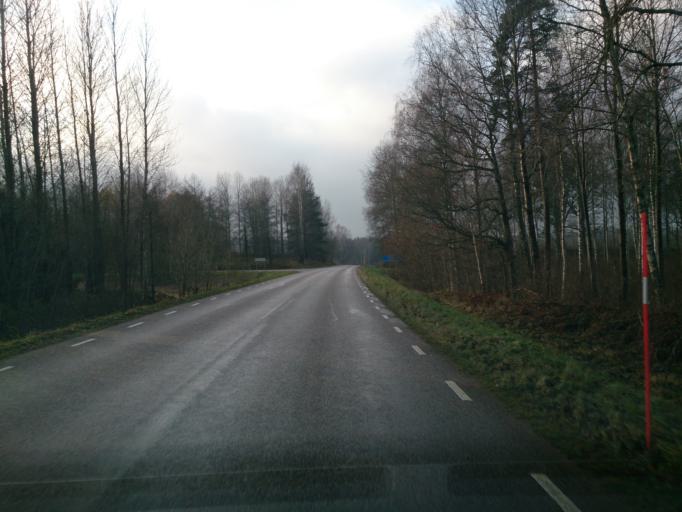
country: SE
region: OEstergoetland
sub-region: Atvidabergs Kommun
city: Atvidaberg
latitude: 58.2216
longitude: 15.9796
